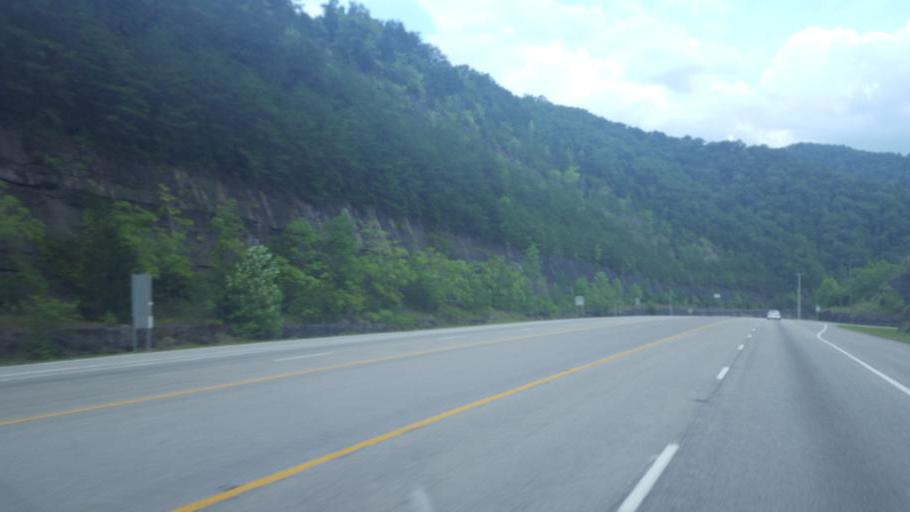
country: US
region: Kentucky
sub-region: Pike County
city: Pikeville
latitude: 37.3785
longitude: -82.5406
